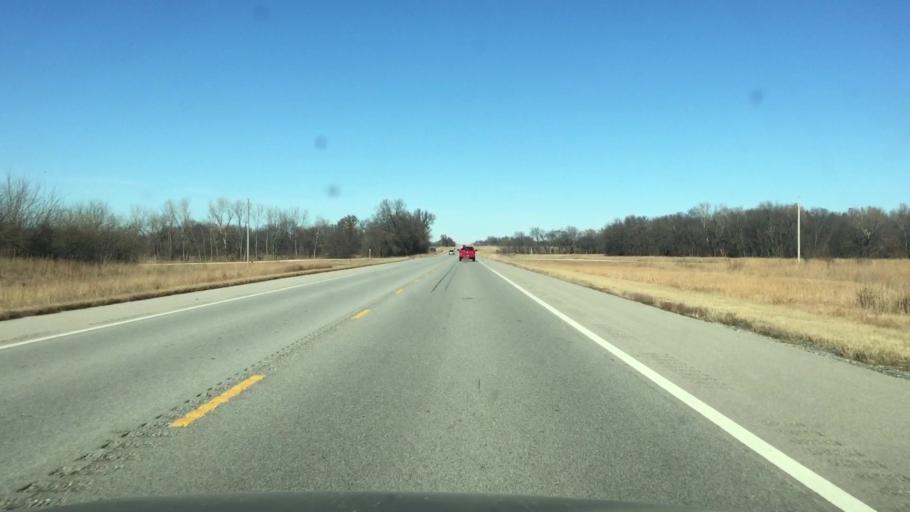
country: US
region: Kansas
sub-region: Allen County
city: Iola
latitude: 37.9789
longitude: -95.3810
